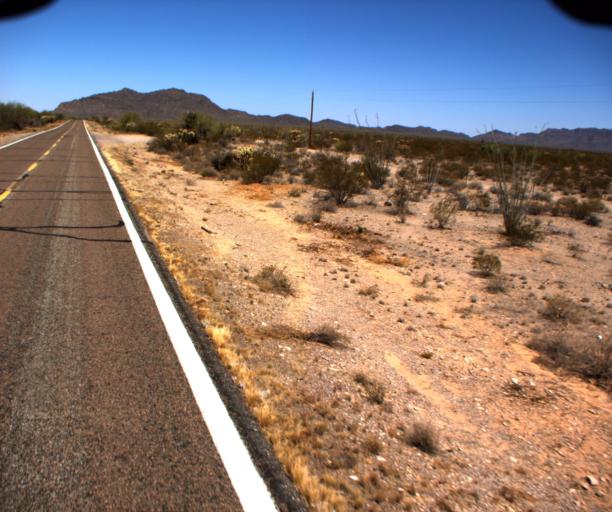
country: US
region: Arizona
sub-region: Pima County
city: Ajo
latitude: 32.2159
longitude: -112.6424
